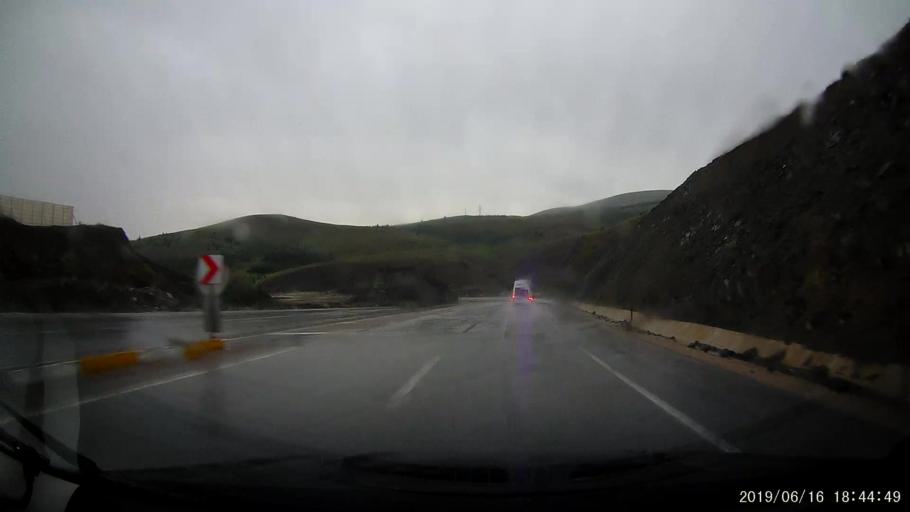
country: TR
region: Erzincan
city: Doganbeyli
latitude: 39.8702
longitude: 39.0664
